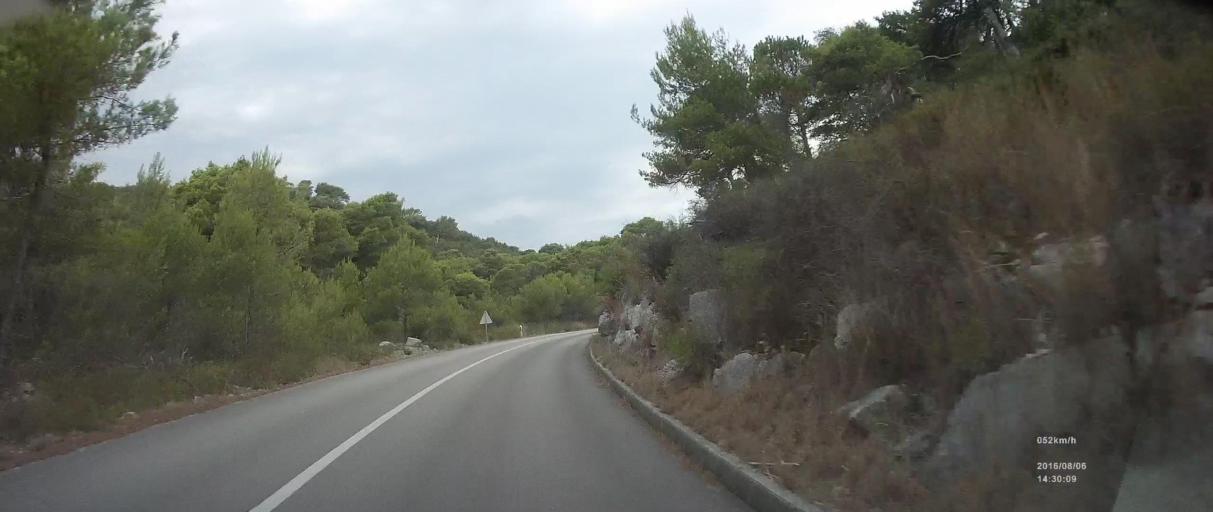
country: HR
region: Dubrovacko-Neretvanska
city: Ston
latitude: 42.7086
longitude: 17.7294
